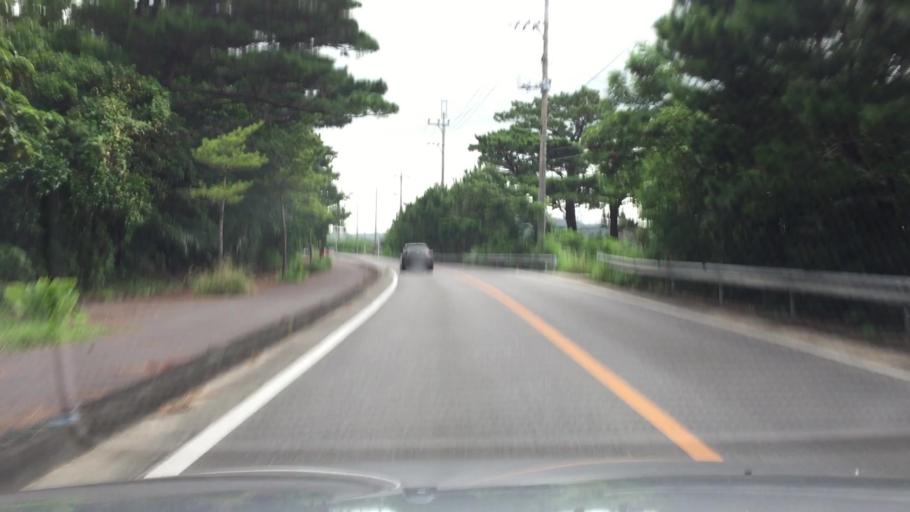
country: JP
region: Okinawa
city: Ishigaki
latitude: 24.4423
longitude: 124.1208
